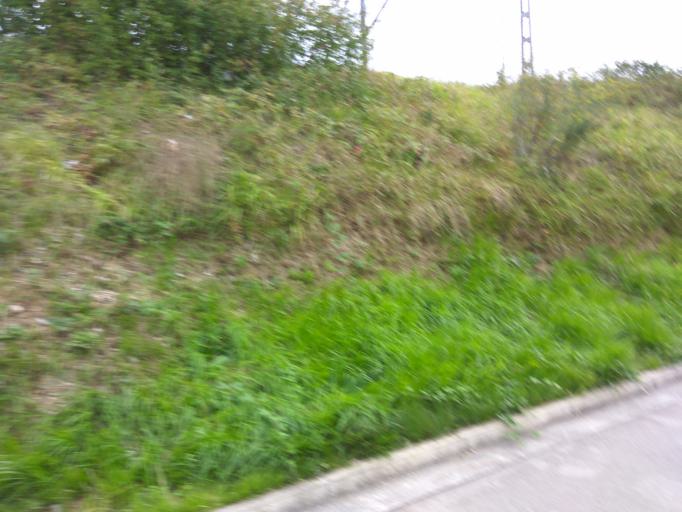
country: ES
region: Basque Country
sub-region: Provincia de Guipuzcoa
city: Villabona
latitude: 43.1924
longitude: -2.0552
